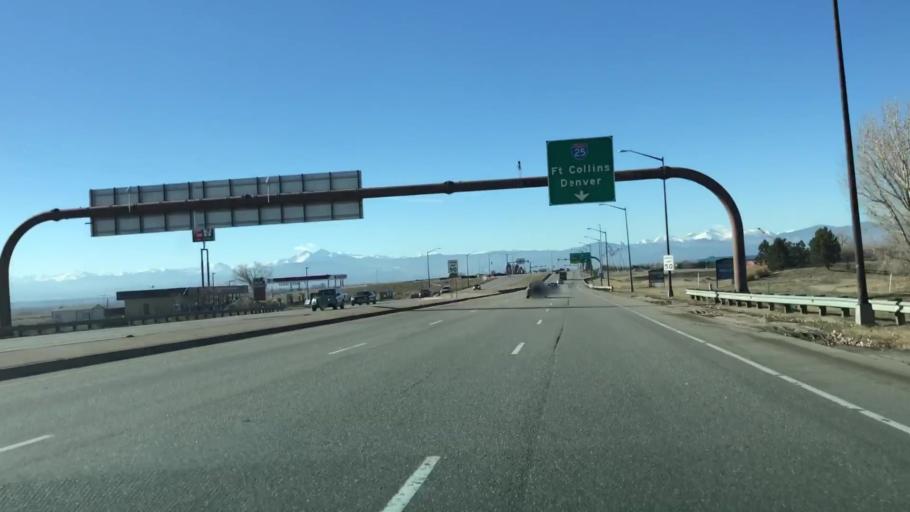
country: US
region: Colorado
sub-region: Larimer County
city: Loveland
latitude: 40.4073
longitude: -104.9867
